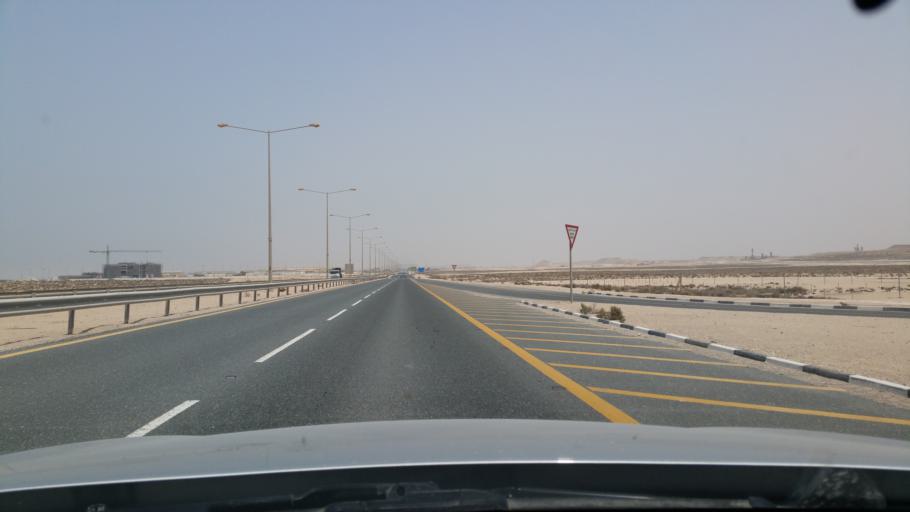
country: QA
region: Baladiyat ar Rayyan
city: Dukhan
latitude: 25.3669
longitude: 50.7804
